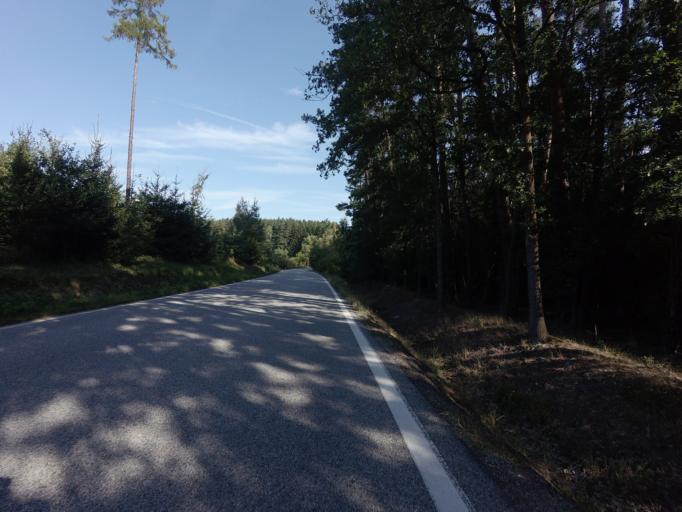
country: CZ
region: Jihocesky
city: Tyn nad Vltavou
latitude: 49.2660
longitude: 14.4111
